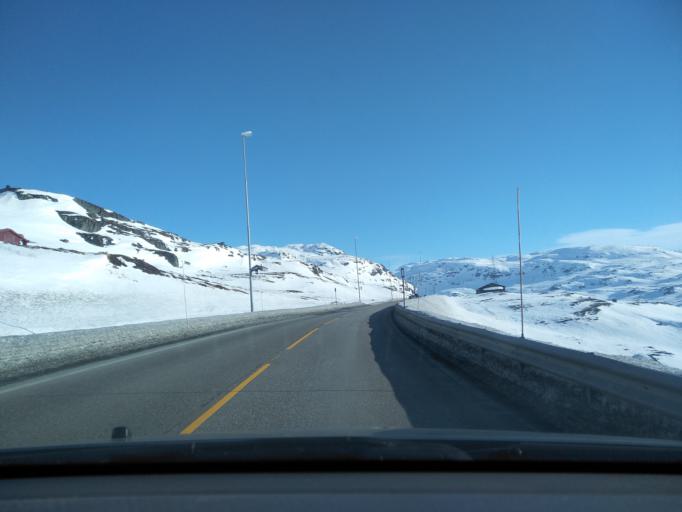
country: NO
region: Aust-Agder
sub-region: Bykle
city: Hovden
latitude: 59.8420
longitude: 6.9789
